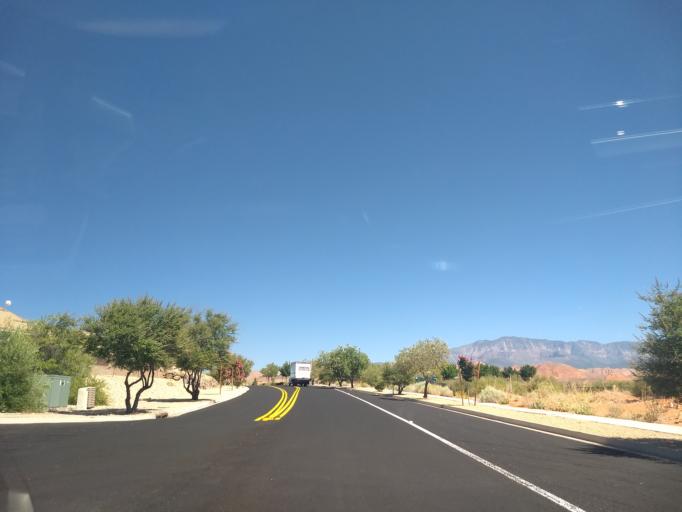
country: US
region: Utah
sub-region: Washington County
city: Washington
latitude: 37.1465
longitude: -113.4640
